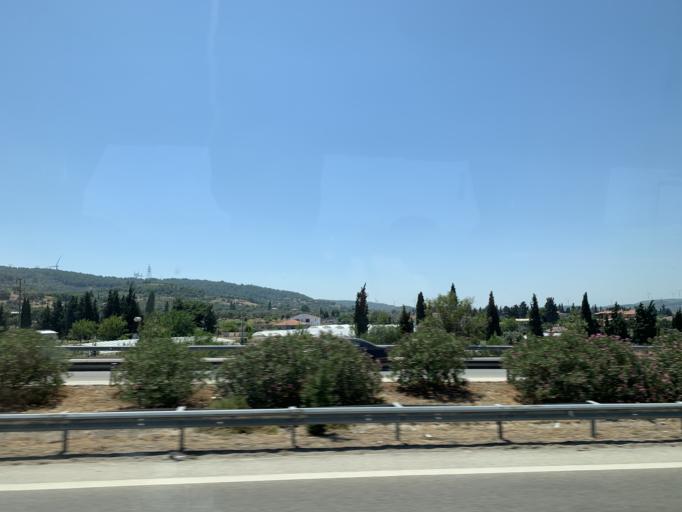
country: TR
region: Izmir
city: Urla
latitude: 38.3030
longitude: 26.7515
